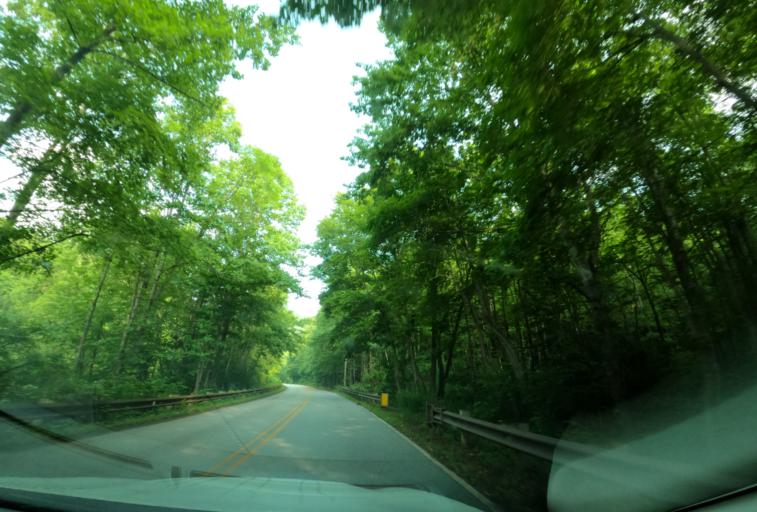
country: US
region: North Carolina
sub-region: Transylvania County
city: Brevard
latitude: 35.2470
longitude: -82.8847
